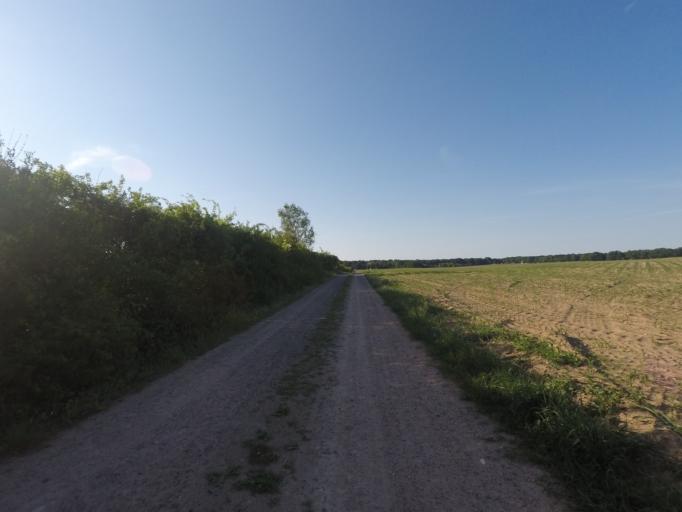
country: DE
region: Brandenburg
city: Joachimsthal
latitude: 52.8973
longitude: 13.7044
